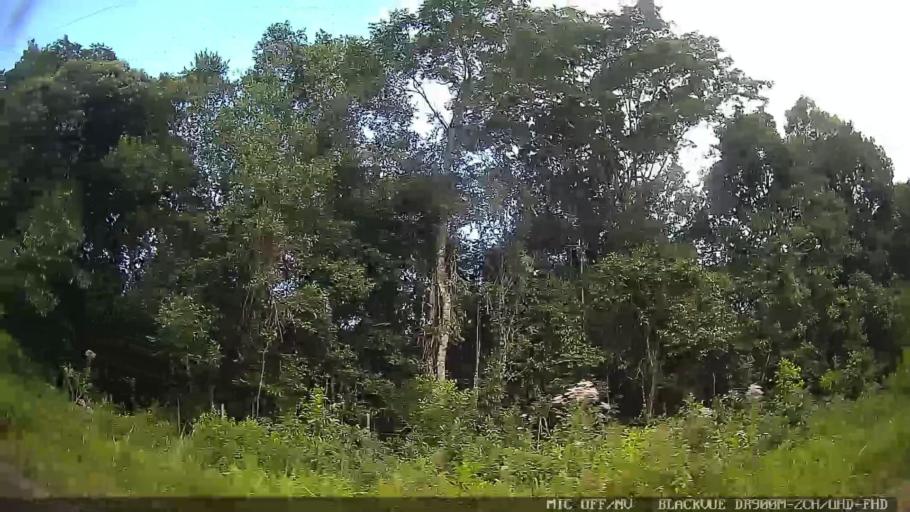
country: BR
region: Sao Paulo
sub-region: Itanhaem
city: Itanhaem
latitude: -24.1734
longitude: -46.9307
